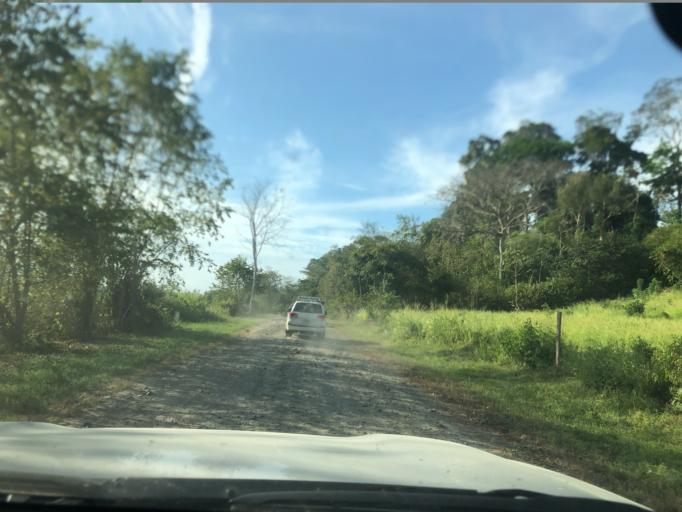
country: CR
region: Alajuela
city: San Jose
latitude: 11.1195
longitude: -85.2856
